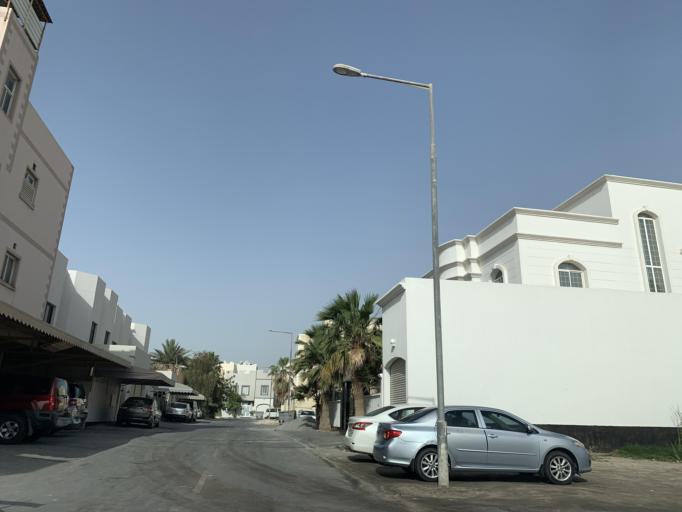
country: BH
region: Northern
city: Madinat `Isa
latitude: 26.1822
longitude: 50.5648
